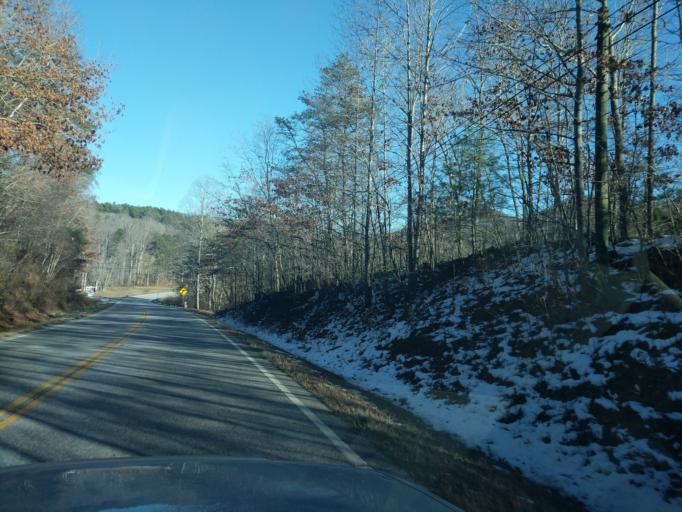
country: US
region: Georgia
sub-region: Towns County
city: Hiawassee
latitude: 34.9254
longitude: -83.6792
